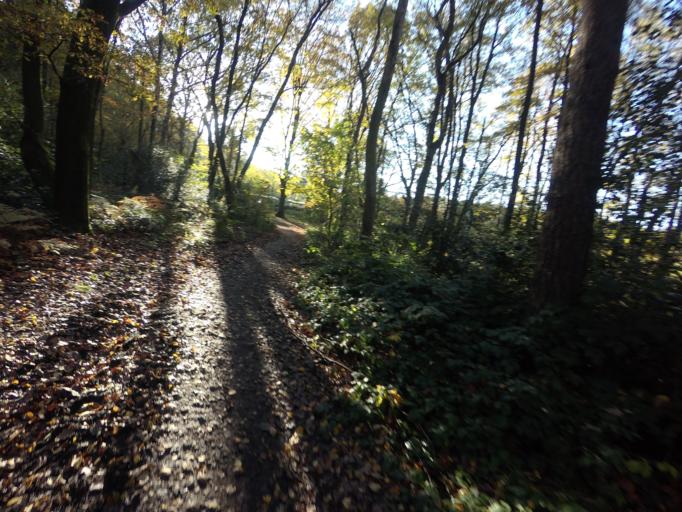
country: BE
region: Wallonia
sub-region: Province de Liege
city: Plombieres
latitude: 50.7727
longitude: 5.9667
